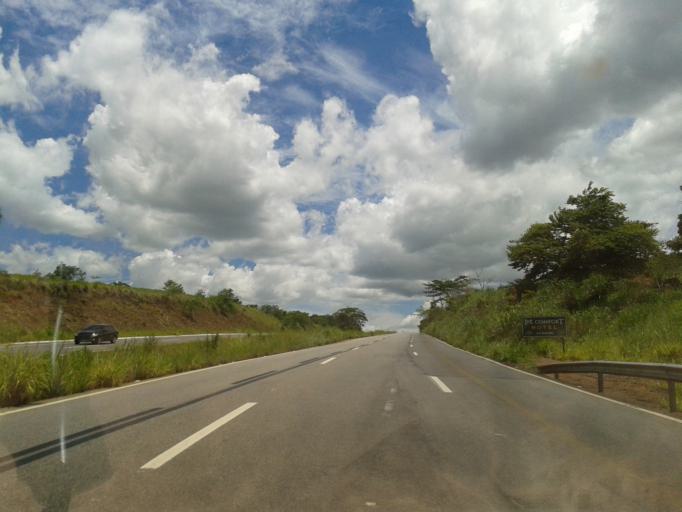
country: BR
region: Goias
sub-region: Neropolis
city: Neropolis
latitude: -16.3565
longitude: -49.2448
